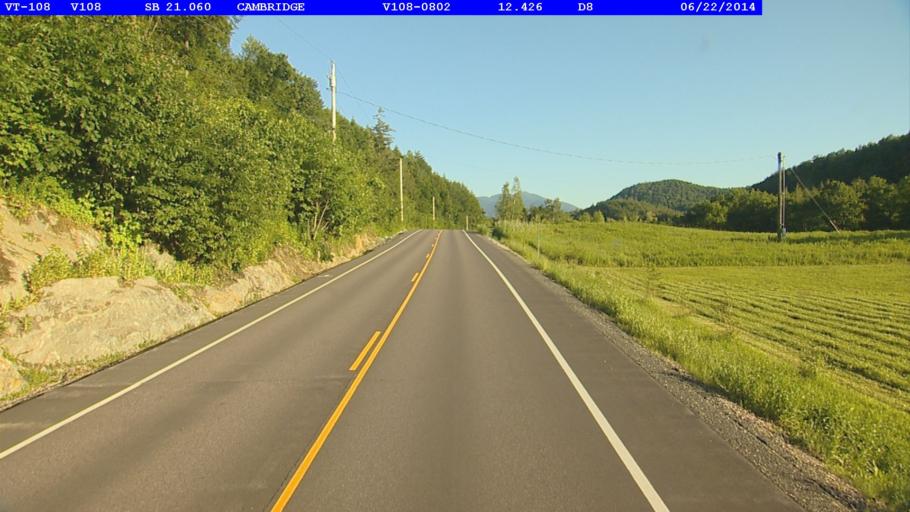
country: US
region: Vermont
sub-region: Lamoille County
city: Johnson
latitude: 44.6941
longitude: -72.8274
